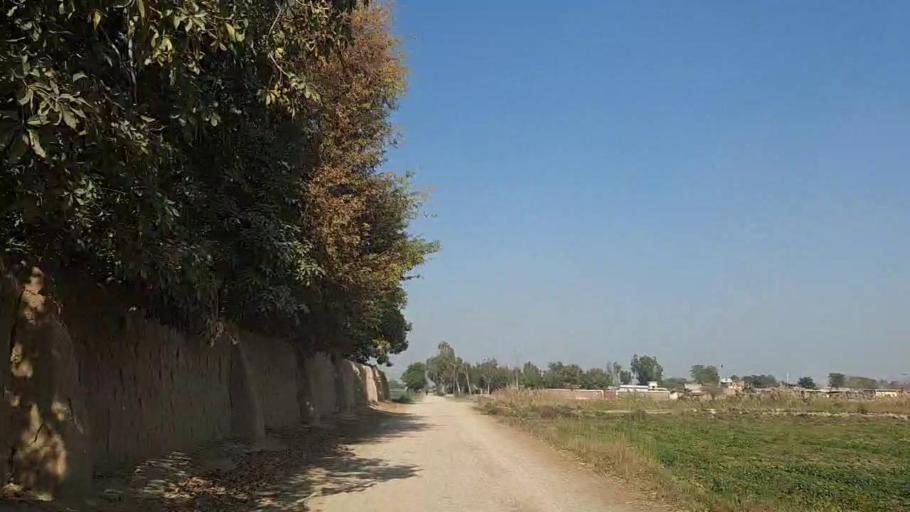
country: PK
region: Sindh
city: Nawabshah
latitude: 26.2454
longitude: 68.3384
